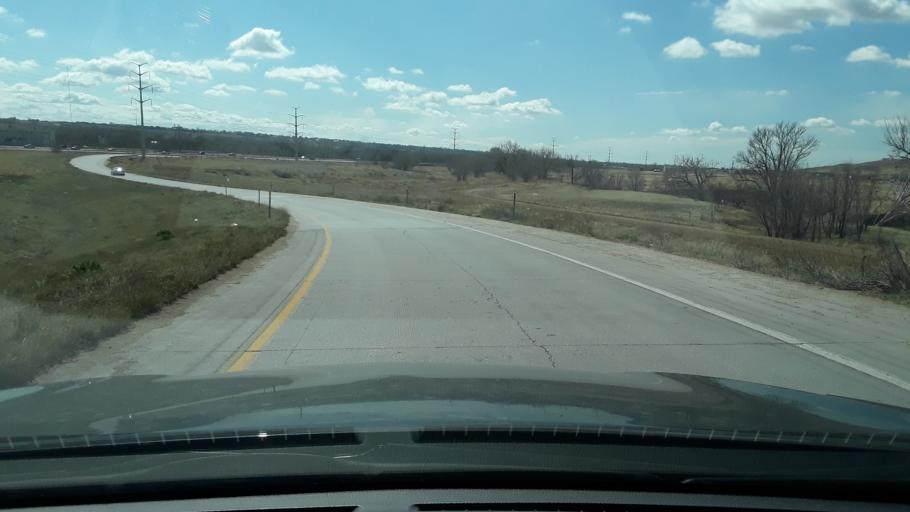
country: US
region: Colorado
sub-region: El Paso County
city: Security-Widefield
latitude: 38.7226
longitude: -104.7346
